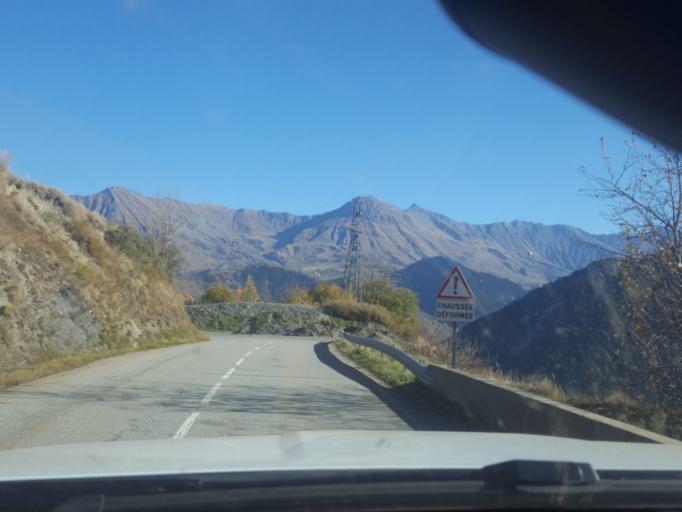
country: FR
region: Rhone-Alpes
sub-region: Departement de la Savoie
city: Saint-Jean-de-Maurienne
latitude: 45.2487
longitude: 6.2885
